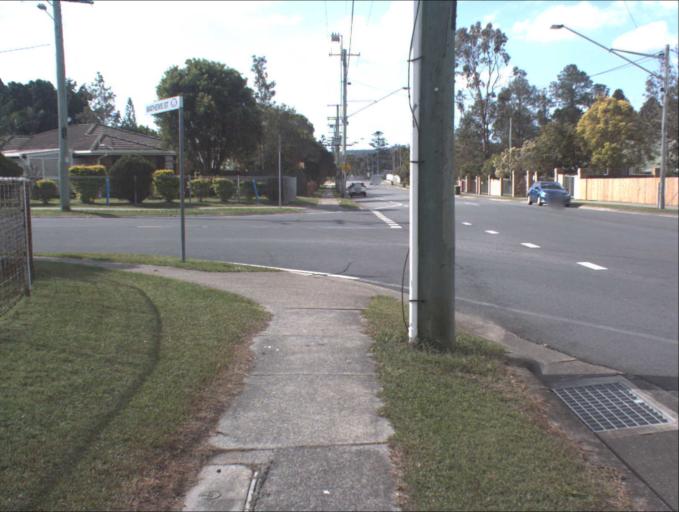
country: AU
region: Queensland
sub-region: Logan
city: Waterford West
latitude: -27.6901
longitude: 153.1570
